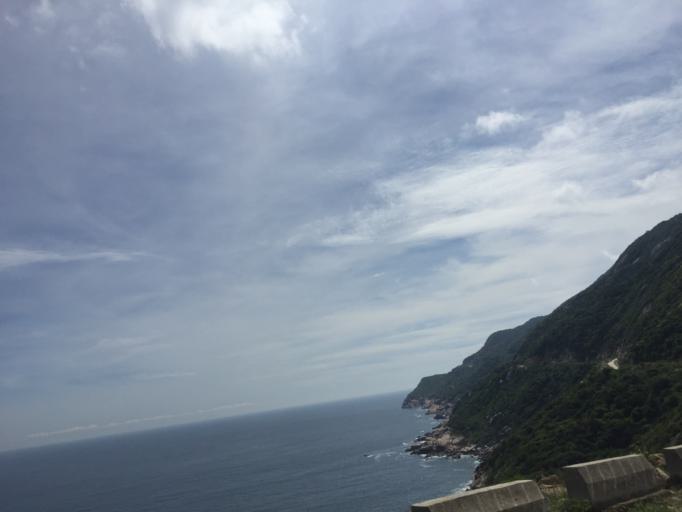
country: VN
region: Quang Nam
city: Hoi An
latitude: 15.9652
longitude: 108.5101
